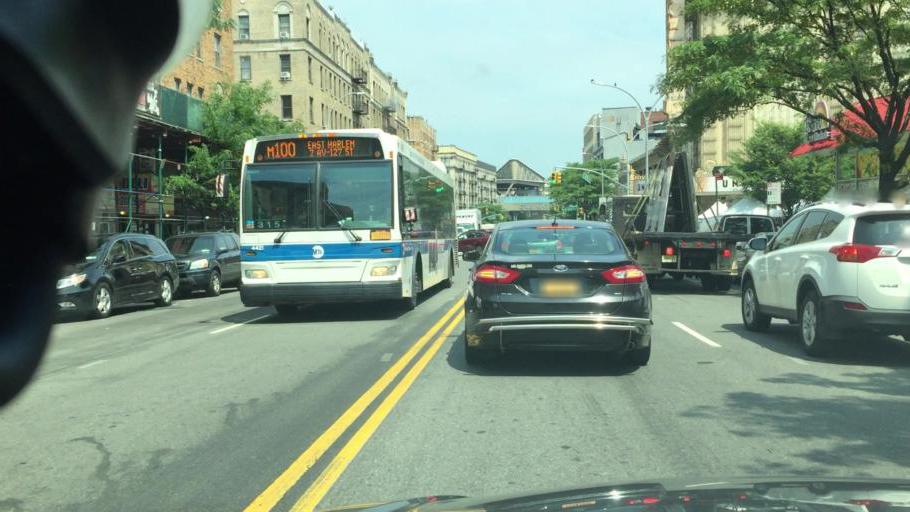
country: US
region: New York
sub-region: New York County
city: Inwood
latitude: 40.8457
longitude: -73.9388
